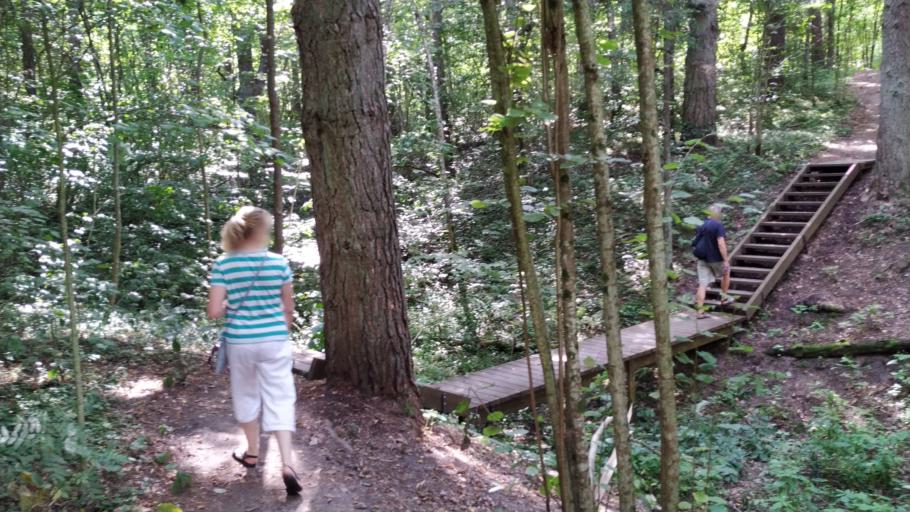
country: LT
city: Grigiskes
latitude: 54.7980
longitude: 24.9812
